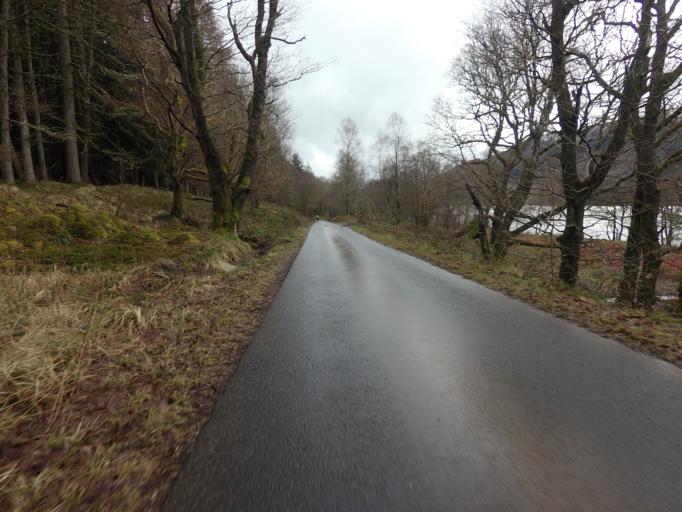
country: GB
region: Scotland
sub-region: West Dunbartonshire
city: Balloch
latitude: 56.2246
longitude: -4.5526
